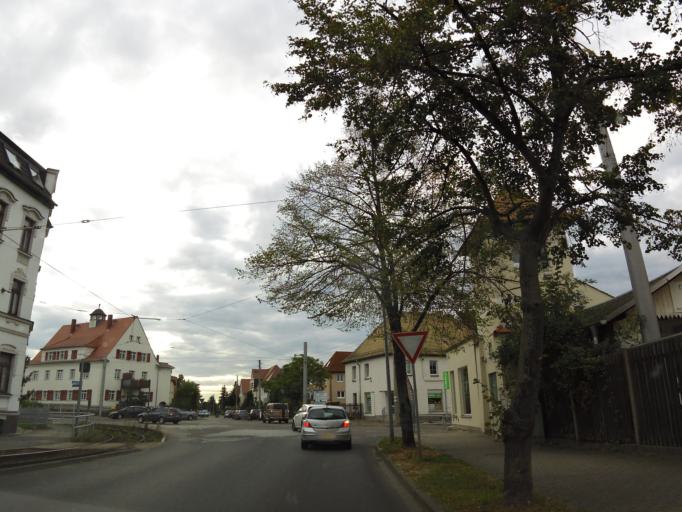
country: DE
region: Saxony
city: Schkeuditz
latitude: 51.3618
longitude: 12.2717
